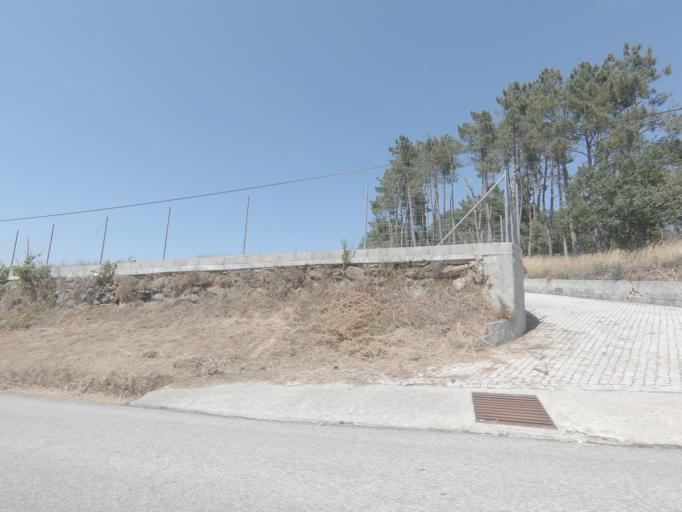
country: PT
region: Viseu
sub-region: Tarouca
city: Tarouca
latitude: 40.9901
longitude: -7.8122
